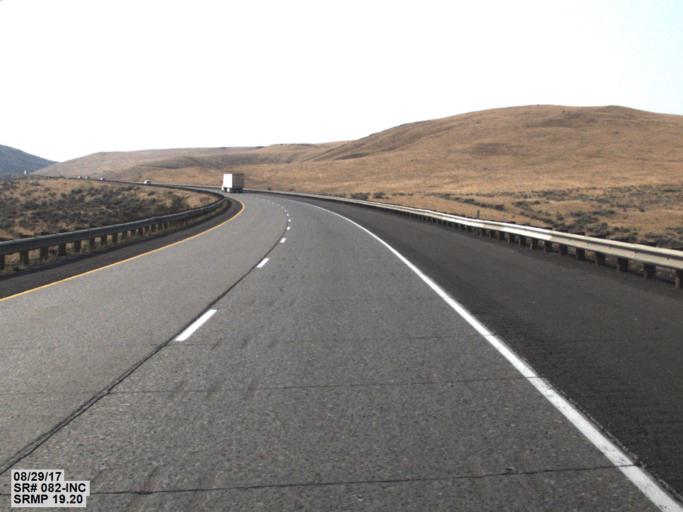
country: US
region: Washington
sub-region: Yakima County
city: Terrace Heights
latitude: 46.7470
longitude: -120.3906
